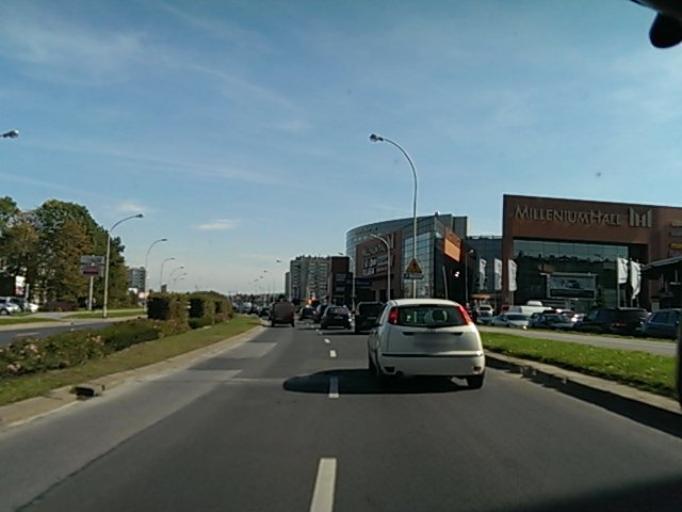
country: PL
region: Subcarpathian Voivodeship
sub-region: Rzeszow
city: Rzeszow
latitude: 50.0285
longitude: 22.0113
